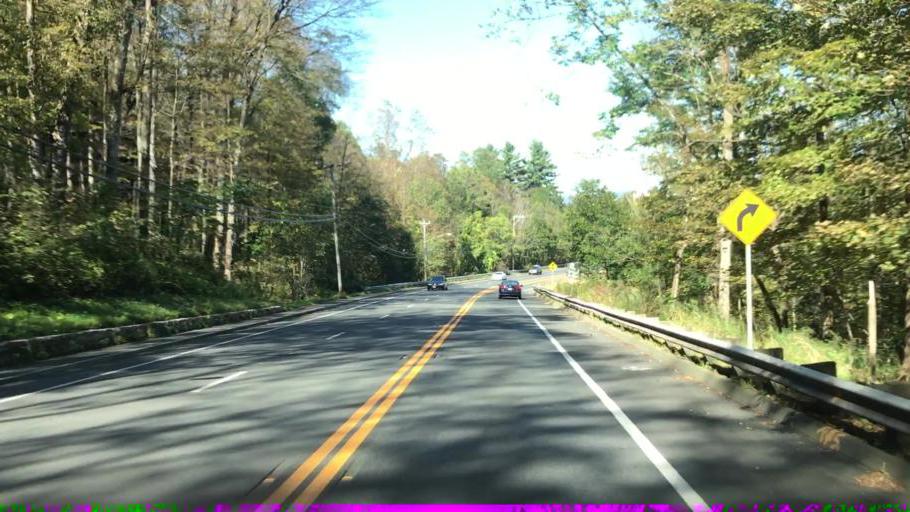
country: US
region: Massachusetts
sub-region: Berkshire County
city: Pittsfield
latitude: 42.4217
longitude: -73.2607
